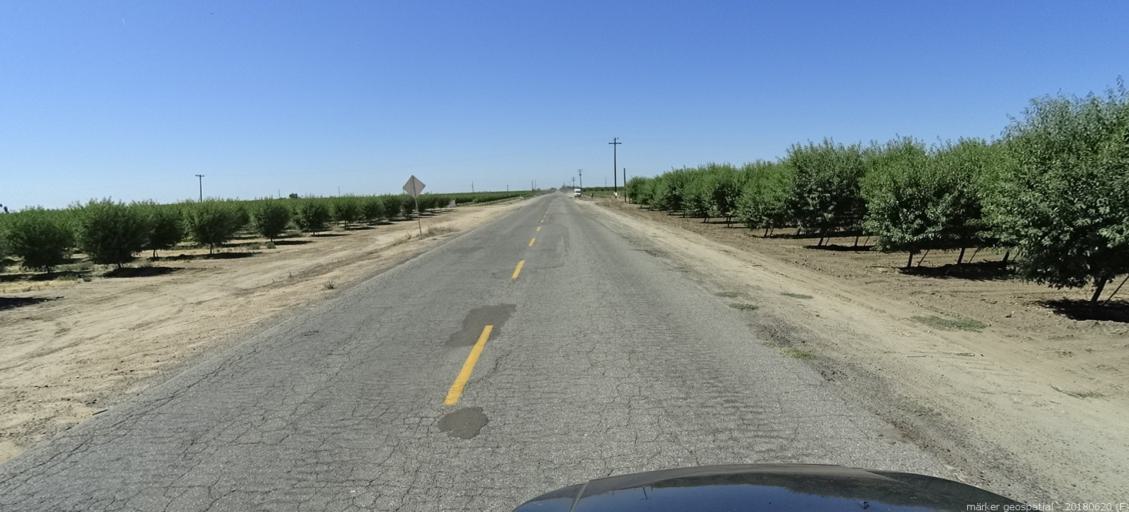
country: US
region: California
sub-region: Madera County
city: Parkwood
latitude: 36.9149
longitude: -120.0194
